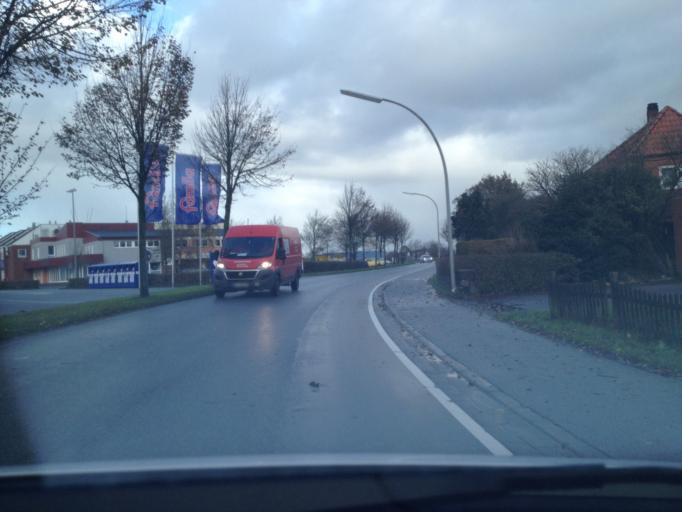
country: DE
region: Schleswig-Holstein
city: Leck
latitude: 54.7764
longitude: 8.9816
